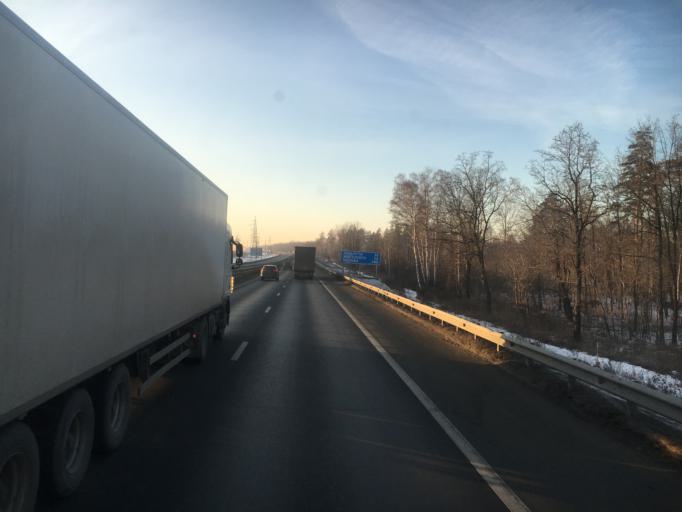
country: RU
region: Samara
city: Pribrezhnyy
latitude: 53.5181
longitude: 49.8294
